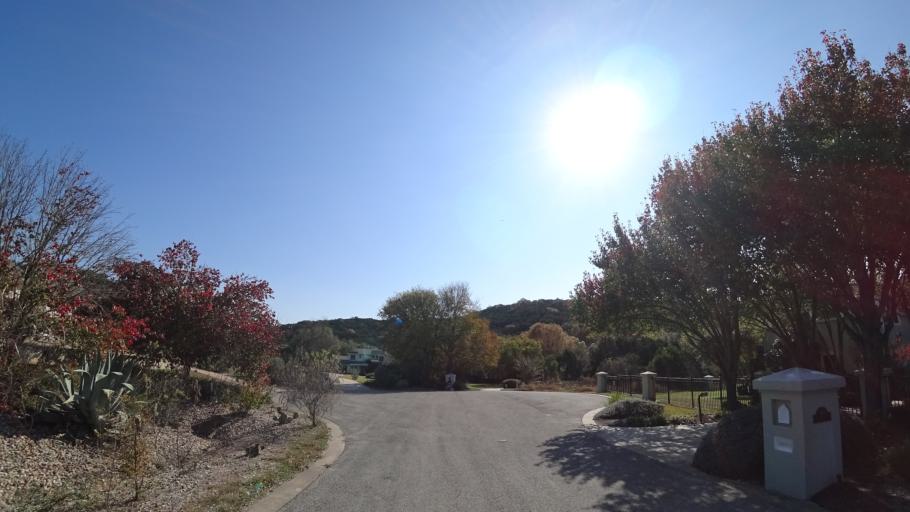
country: US
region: Texas
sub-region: Travis County
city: West Lake Hills
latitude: 30.3694
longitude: -97.8239
